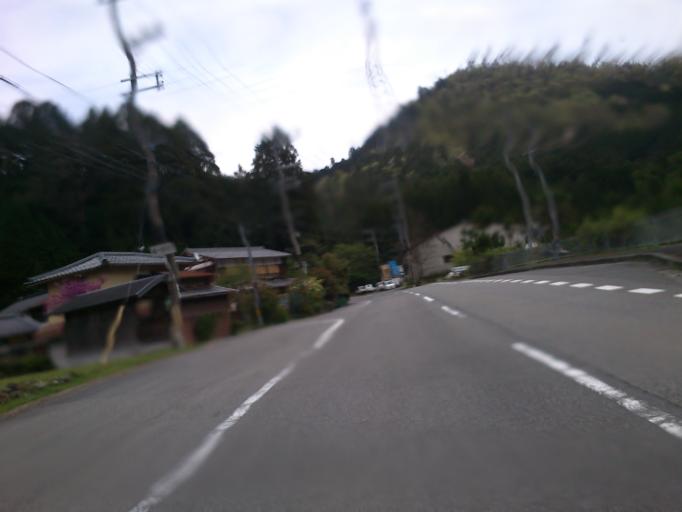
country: JP
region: Kyoto
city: Kameoka
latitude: 35.2052
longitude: 135.6146
